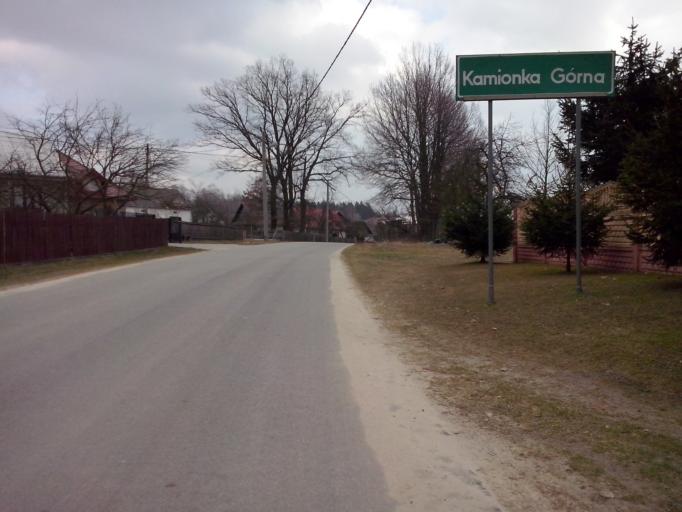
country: PL
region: Subcarpathian Voivodeship
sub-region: Powiat nizanski
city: Krzeszow
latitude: 50.4272
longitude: 22.3392
